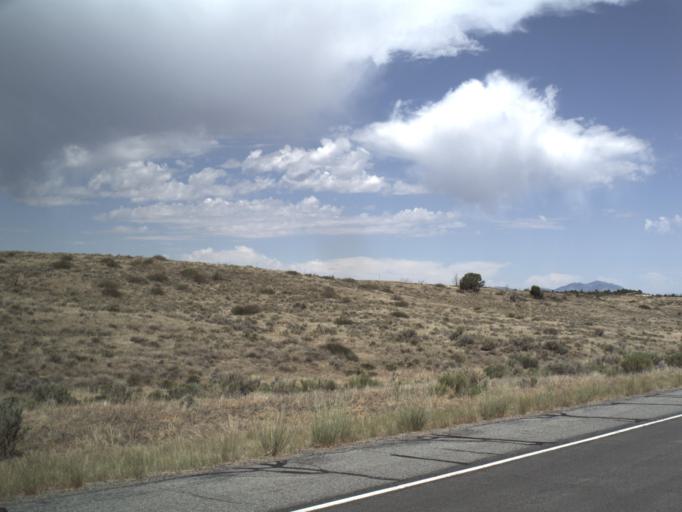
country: US
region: Utah
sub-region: Utah County
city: Genola
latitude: 39.9764
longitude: -112.2594
